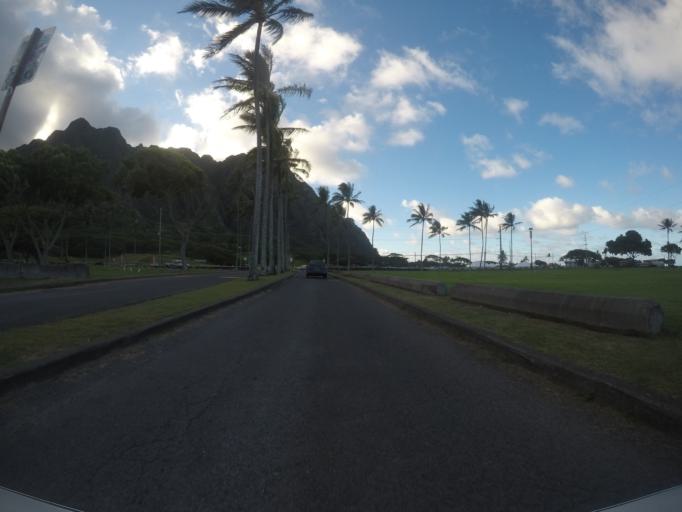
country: US
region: Hawaii
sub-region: Honolulu County
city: Ka'a'awa
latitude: 21.5163
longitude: -157.8373
